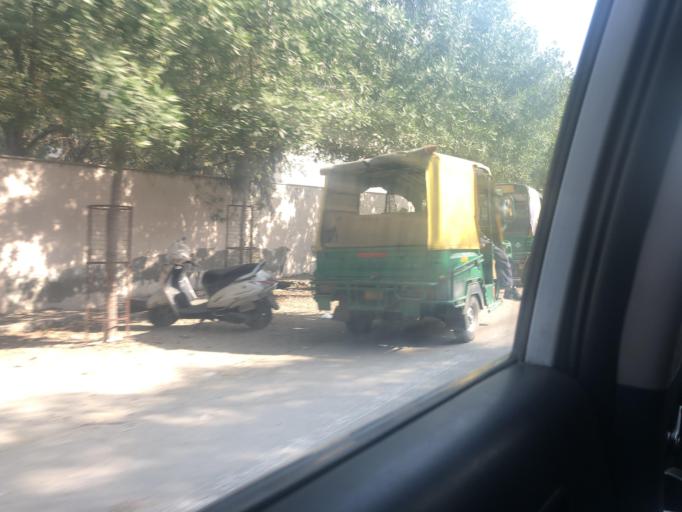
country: IN
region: Haryana
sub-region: Jhajjar
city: Bahadurgarh
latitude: 28.6870
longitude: 76.8892
